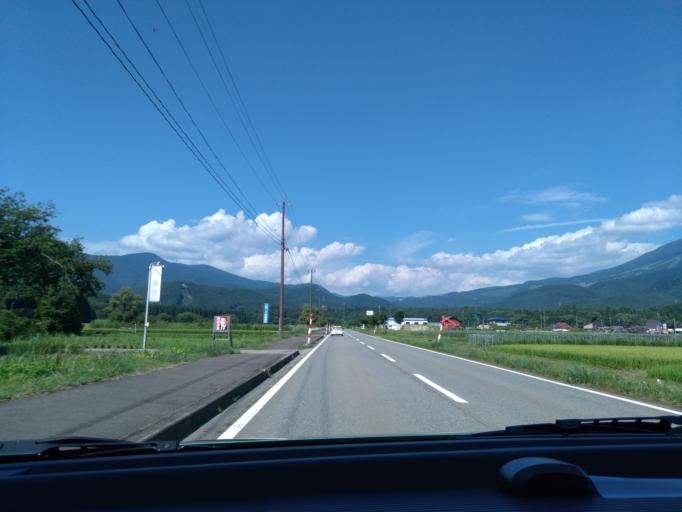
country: JP
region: Akita
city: Kakunodatemachi
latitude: 39.7384
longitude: 140.7102
